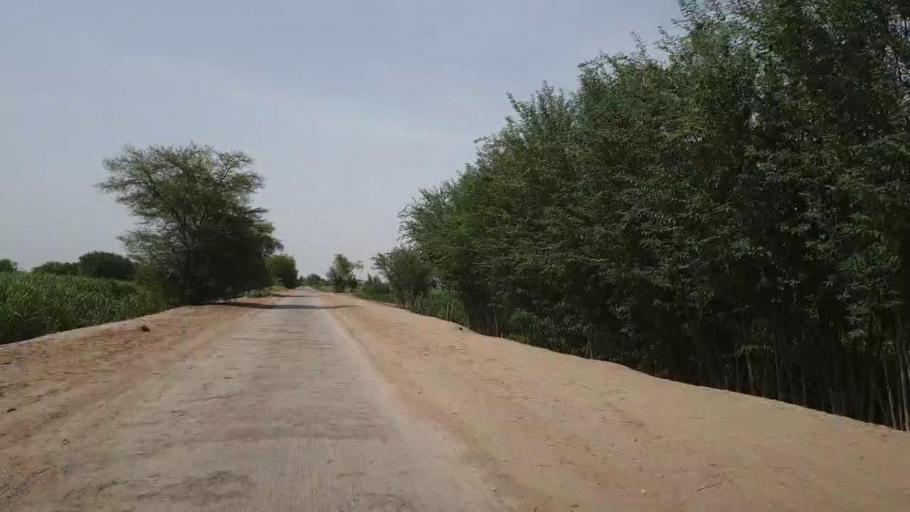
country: PK
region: Sindh
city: Daur
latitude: 26.5326
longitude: 68.4076
